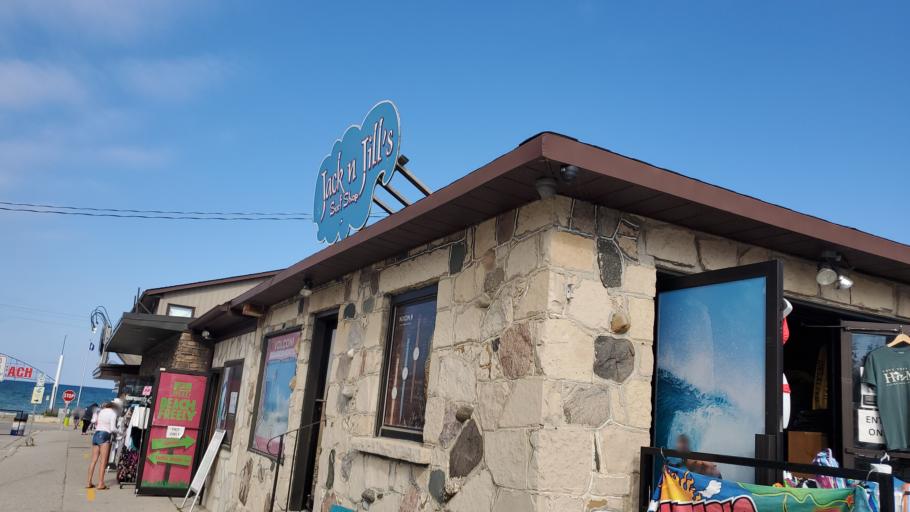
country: CA
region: Ontario
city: Owen Sound
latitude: 44.6295
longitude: -81.2696
